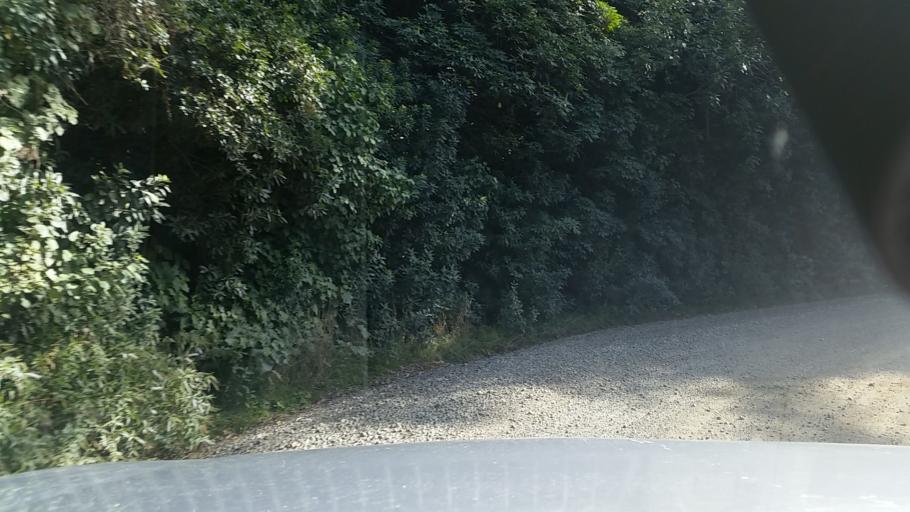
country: NZ
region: Marlborough
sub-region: Marlborough District
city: Picton
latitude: -41.2962
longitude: 174.1236
